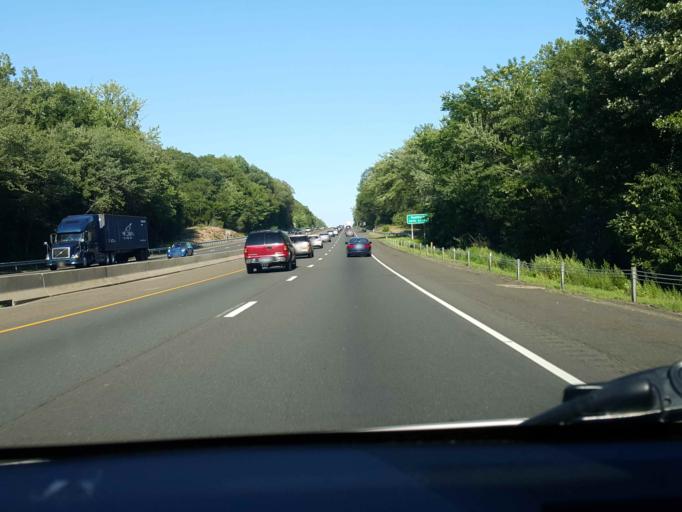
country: US
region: Connecticut
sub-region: New Haven County
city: North Branford
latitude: 41.2970
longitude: -72.7460
